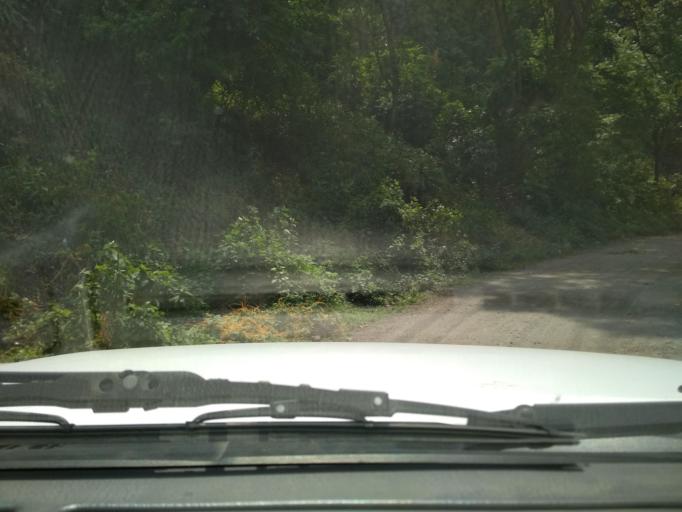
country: MX
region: Veracruz
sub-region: La Perla
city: Metlac Hernandez (Metlac Primero)
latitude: 18.9910
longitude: -97.1196
